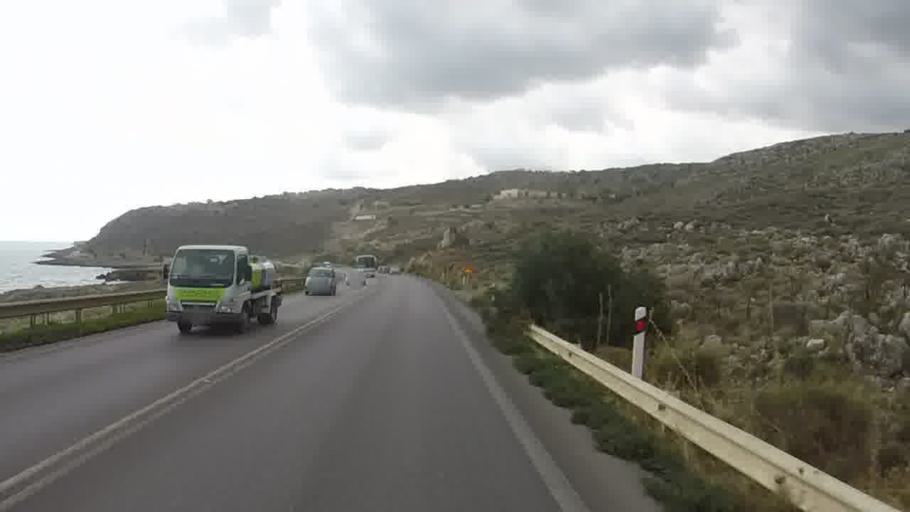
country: GR
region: Crete
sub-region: Nomos Rethymnis
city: Atsipopoulon
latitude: 35.3597
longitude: 24.3872
